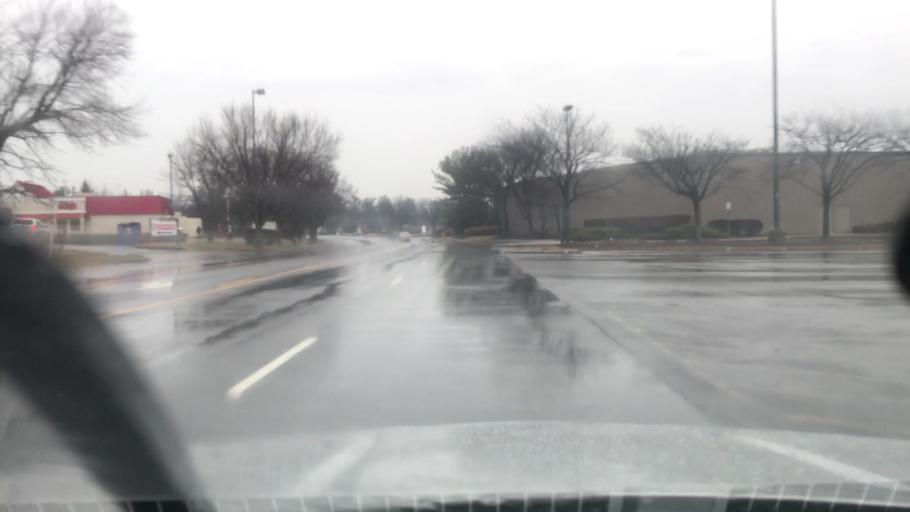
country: US
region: Pennsylvania
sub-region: Bucks County
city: Cornwells Heights
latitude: 40.0888
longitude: -74.9641
